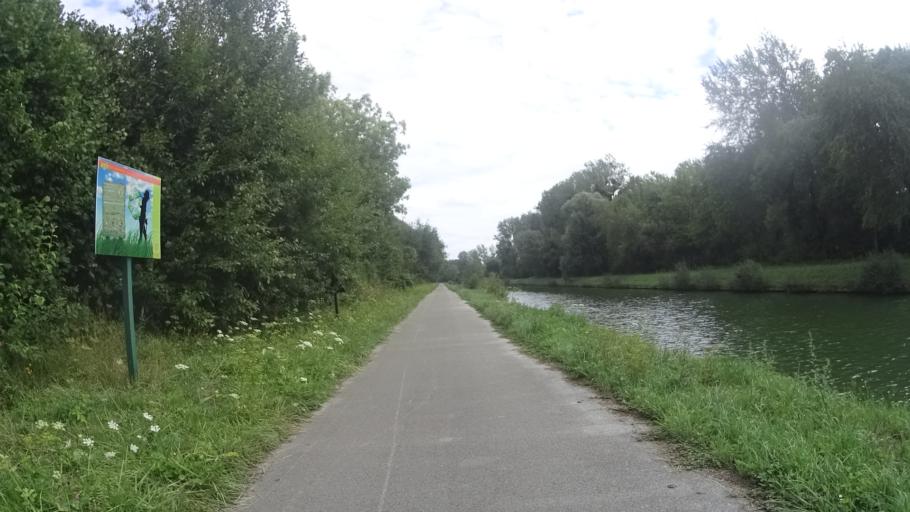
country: FR
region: Picardie
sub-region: Departement de l'Aisne
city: Blerancourt
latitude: 49.5773
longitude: 3.0913
